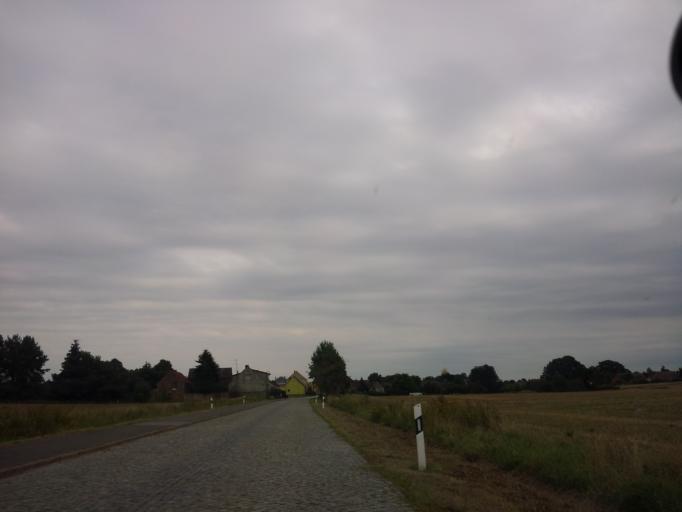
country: DE
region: Brandenburg
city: Niedergorsdorf
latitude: 52.0104
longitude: 12.9321
